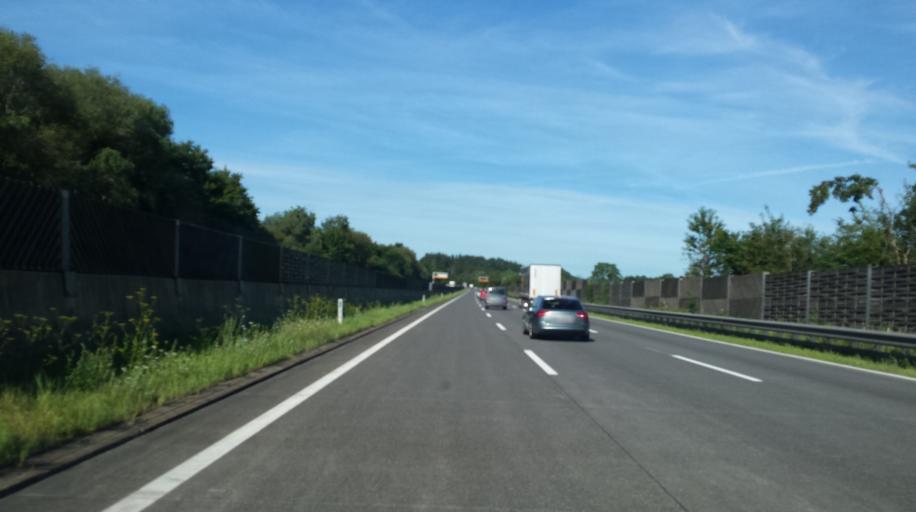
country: AT
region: Upper Austria
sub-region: Politischer Bezirk Vocklabruck
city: Gampern
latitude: 47.9557
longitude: 13.5461
